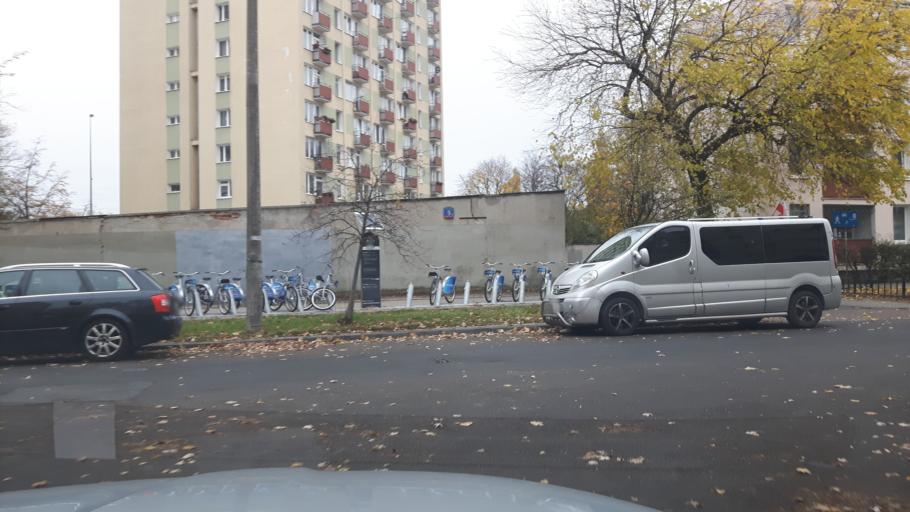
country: PL
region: Masovian Voivodeship
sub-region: Warszawa
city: Praga Polnoc
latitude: 52.2640
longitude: 21.0263
